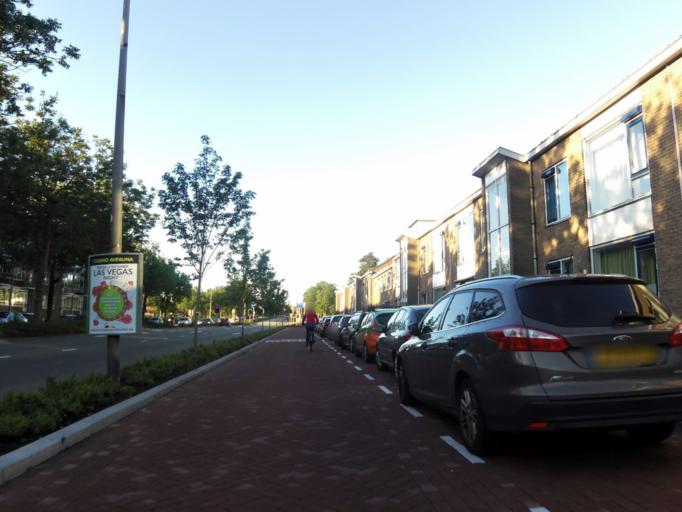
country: NL
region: South Holland
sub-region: Gemeente Alphen aan den Rijn
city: Alphen aan den Rijn
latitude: 52.1378
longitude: 4.6567
